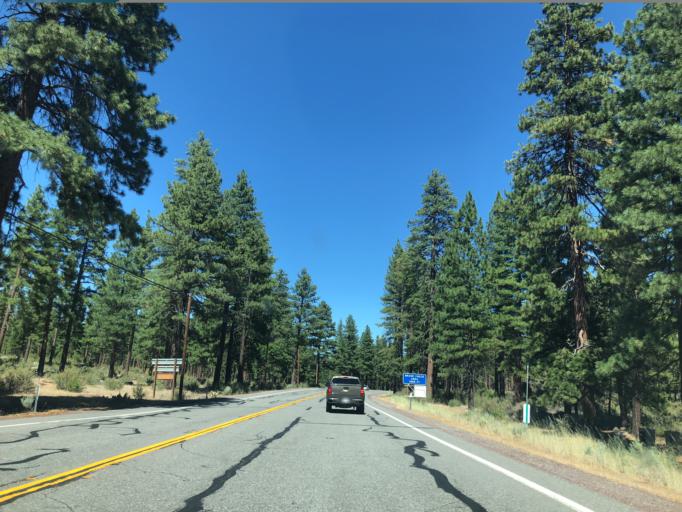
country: US
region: California
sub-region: Lassen County
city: Susanville
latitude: 40.4203
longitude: -120.7028
